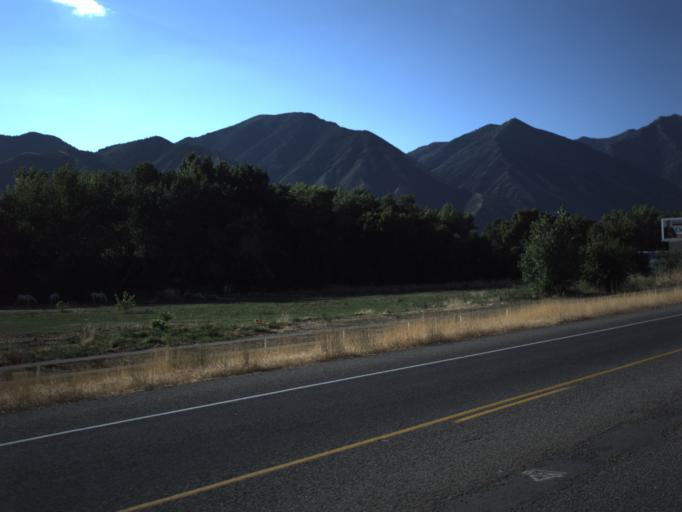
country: US
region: Utah
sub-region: Utah County
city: Spanish Fork
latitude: 40.0894
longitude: -111.6558
